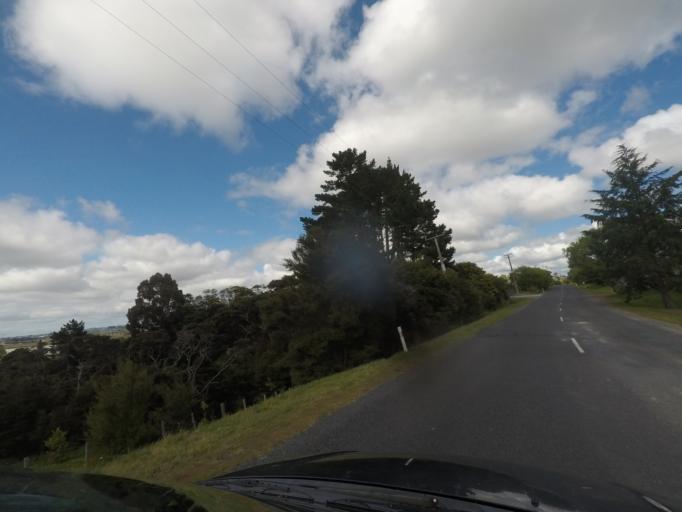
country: NZ
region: Auckland
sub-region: Auckland
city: Rothesay Bay
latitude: -36.7640
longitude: 174.6465
